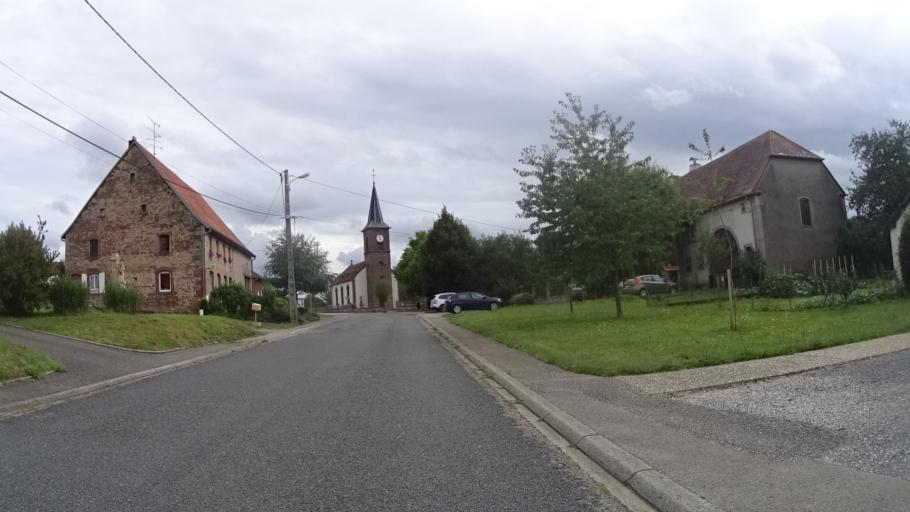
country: FR
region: Lorraine
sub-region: Departement de la Moselle
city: Niderviller
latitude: 48.7050
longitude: 7.0773
